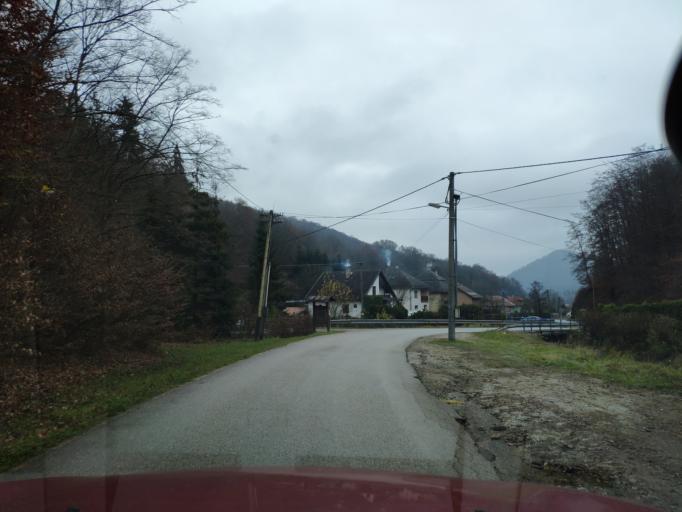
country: SK
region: Kosicky
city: Roznava
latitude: 48.6984
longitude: 20.5472
